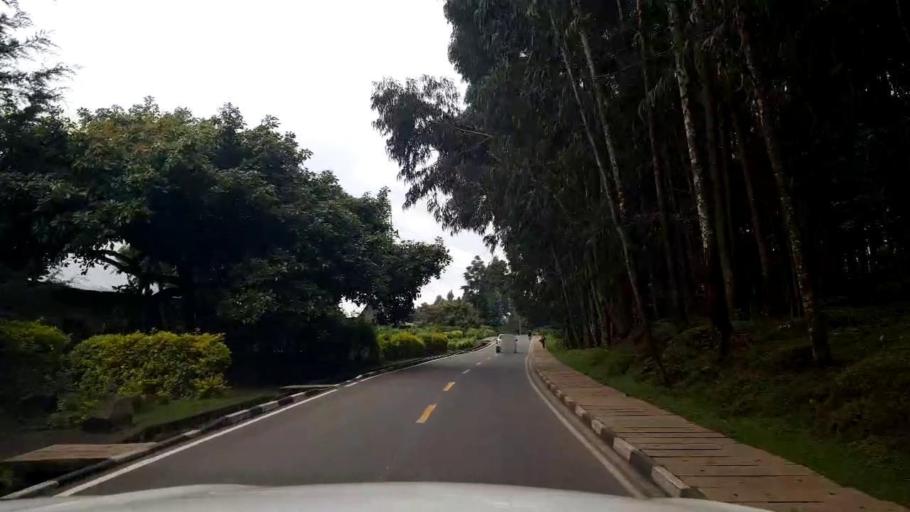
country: RW
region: Northern Province
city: Musanze
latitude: -1.4509
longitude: 29.5941
